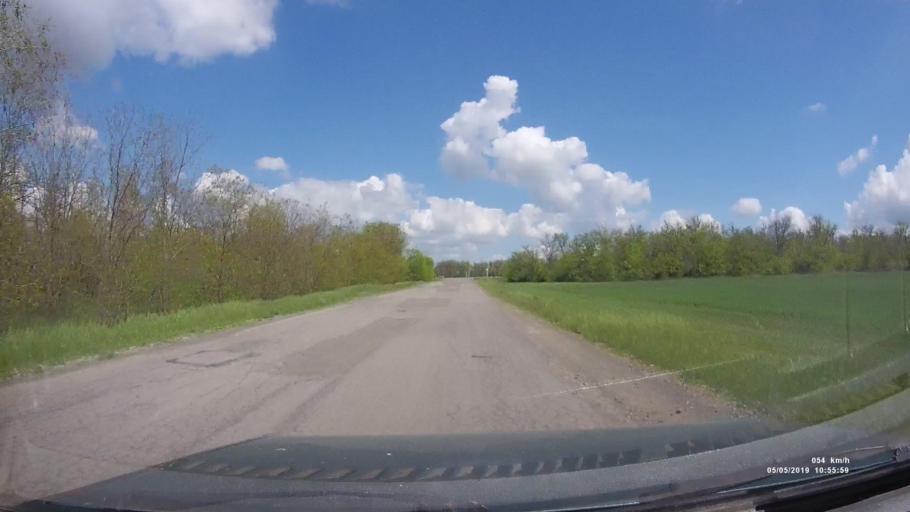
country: RU
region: Rostov
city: Ust'-Donetskiy
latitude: 47.6704
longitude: 40.8197
